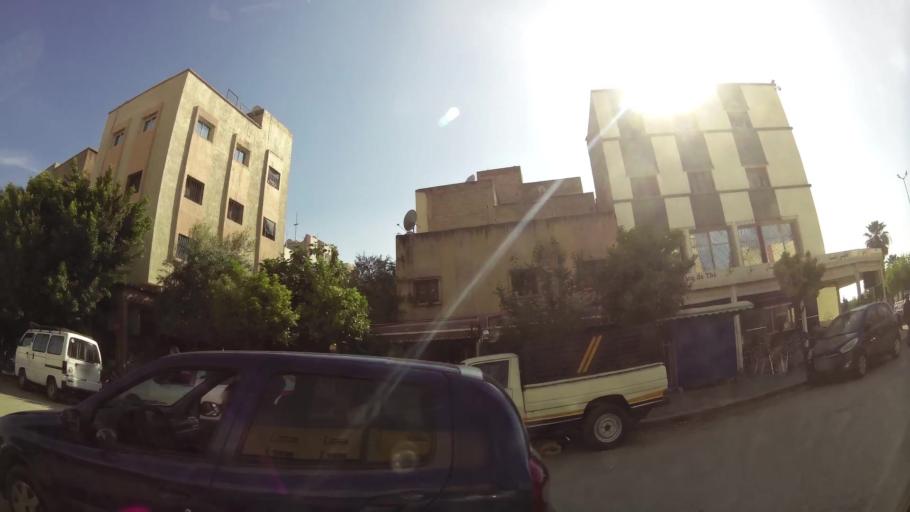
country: MA
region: Fes-Boulemane
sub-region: Fes
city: Fes
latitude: 34.0189
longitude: -5.0340
